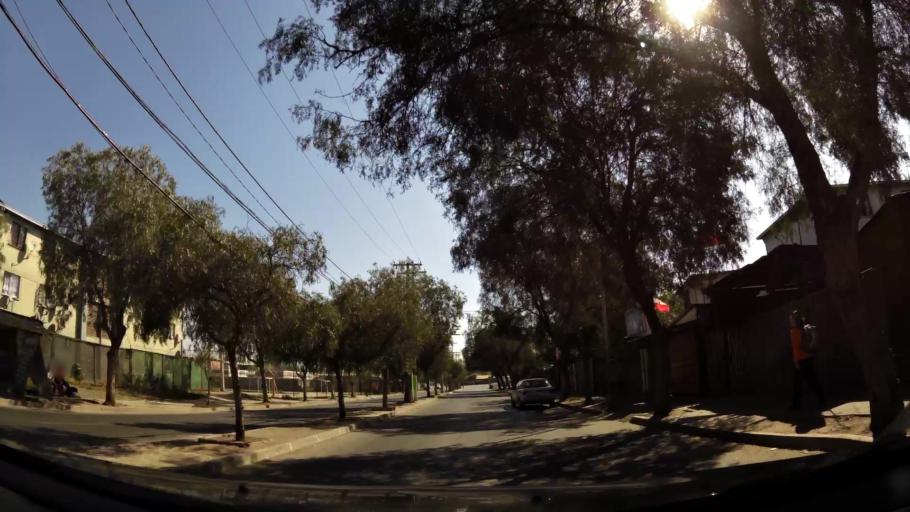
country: CL
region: Santiago Metropolitan
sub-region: Provincia de Santiago
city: La Pintana
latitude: -33.6254
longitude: -70.6267
